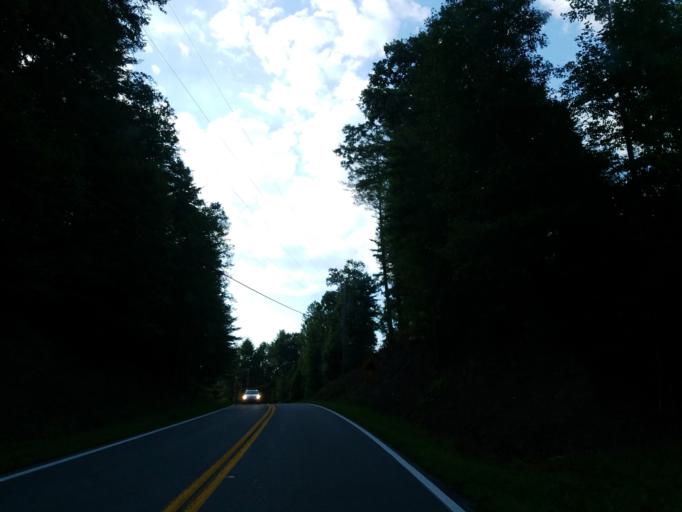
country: US
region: Georgia
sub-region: Fannin County
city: Blue Ridge
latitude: 34.7864
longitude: -84.2669
